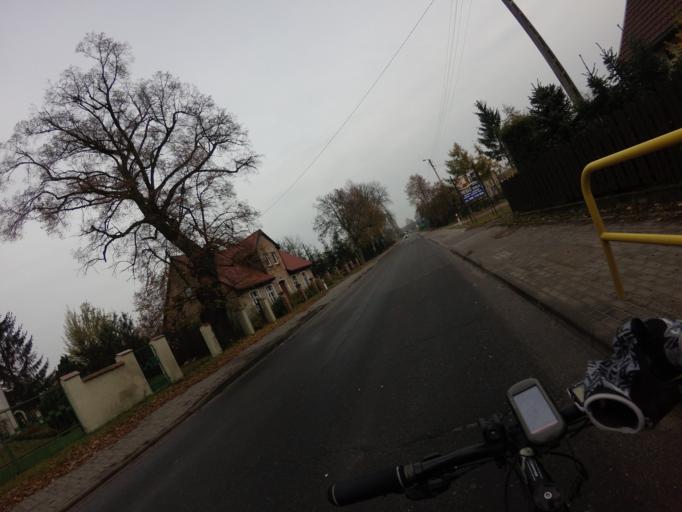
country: PL
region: Kujawsko-Pomorskie
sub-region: Powiat bydgoski
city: Osielsko
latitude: 53.2196
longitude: 18.0590
